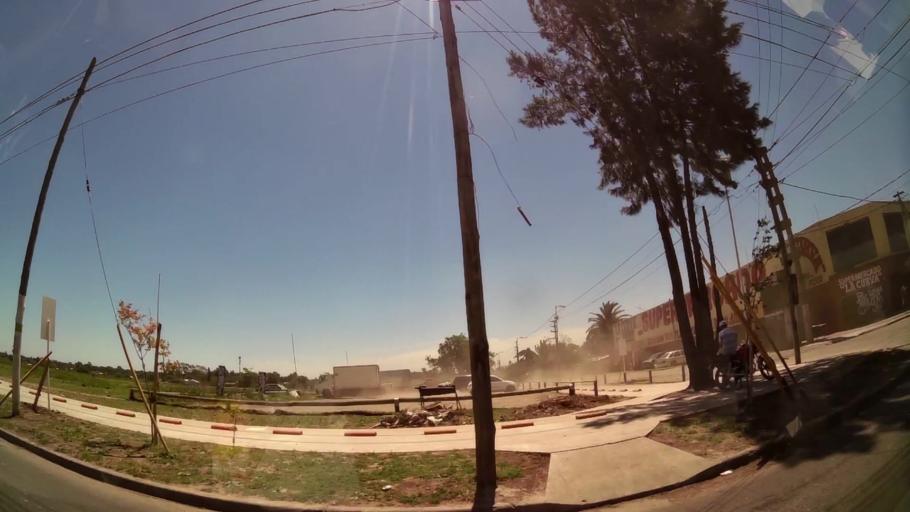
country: AR
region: Buenos Aires
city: Hurlingham
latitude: -34.4943
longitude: -58.6715
